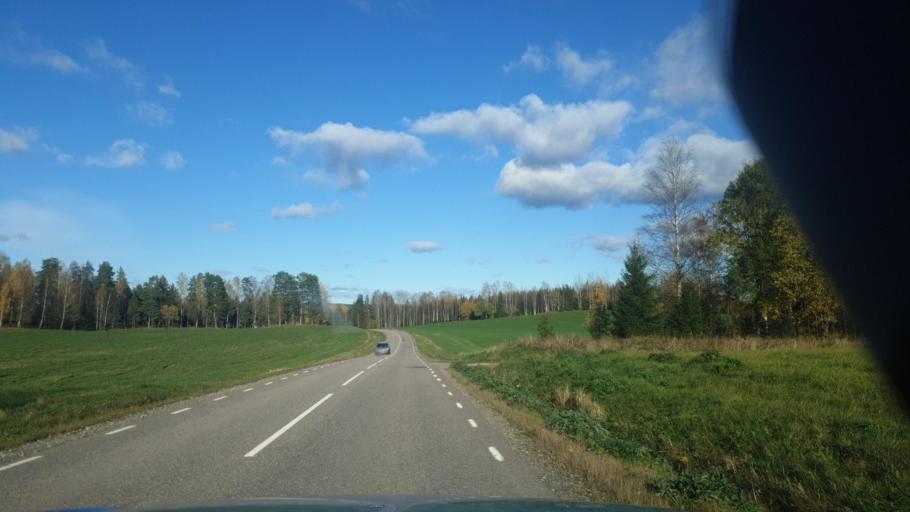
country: SE
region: Vaermland
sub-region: Arvika Kommun
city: Arvika
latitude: 59.6428
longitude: 12.8899
